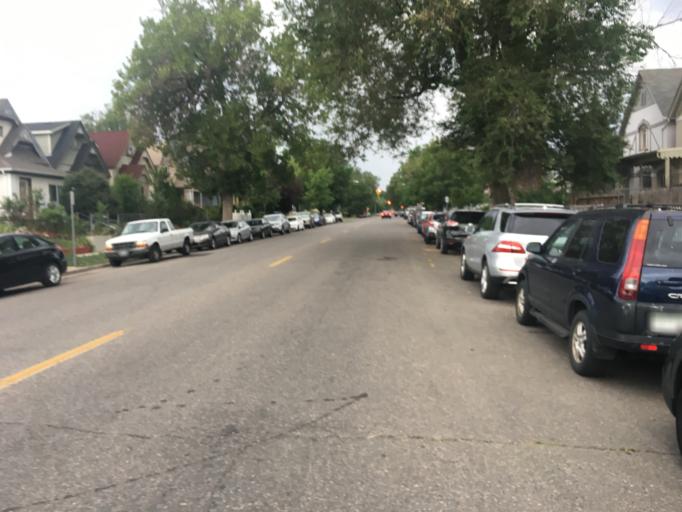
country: US
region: Colorado
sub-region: Denver County
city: Denver
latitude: 39.7631
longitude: -104.9660
